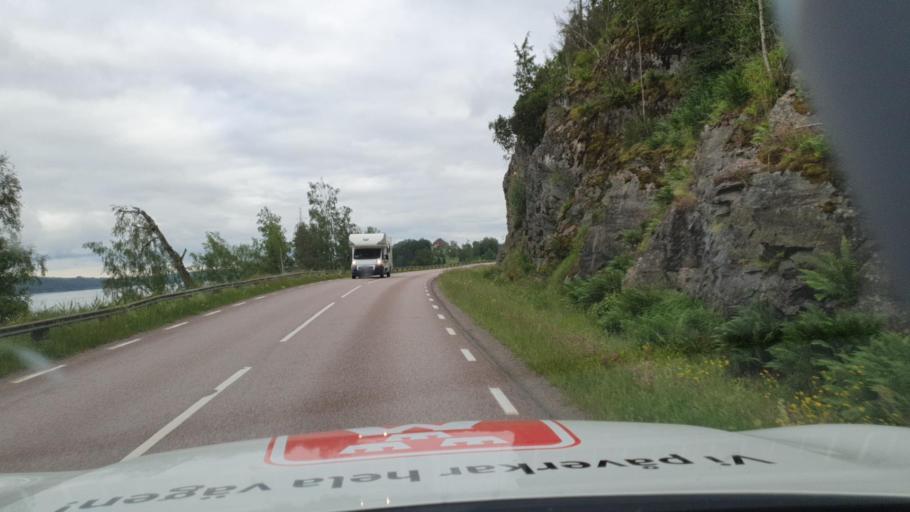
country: SE
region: Vaermland
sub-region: Kils Kommun
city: Kil
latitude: 59.5875
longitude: 13.3147
